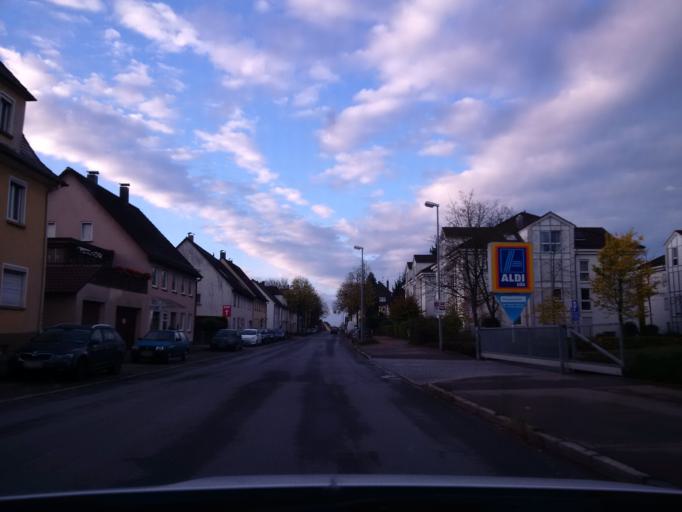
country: DE
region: Baden-Wuerttemberg
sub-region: Tuebingen Region
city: Laupheim
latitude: 48.2347
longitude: 9.8810
